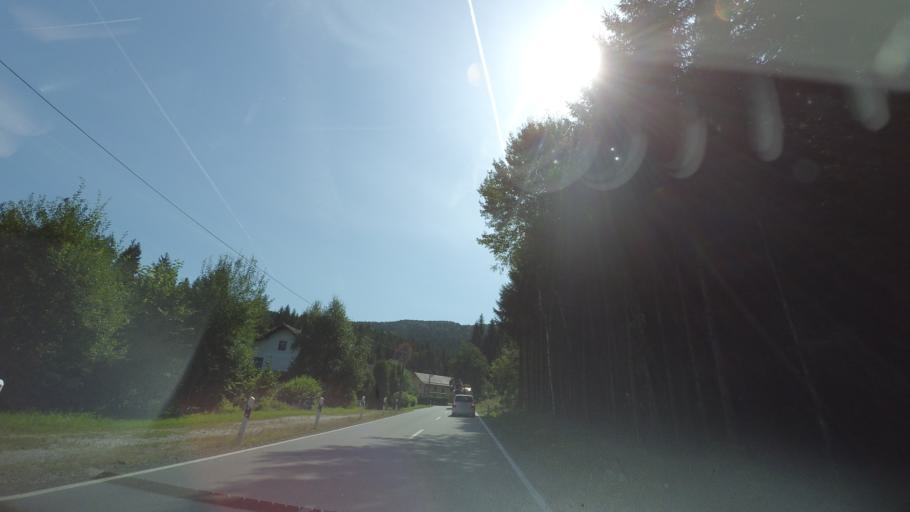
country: DE
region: Bavaria
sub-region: Lower Bavaria
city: Drachselsried
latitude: 49.0870
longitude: 13.0067
